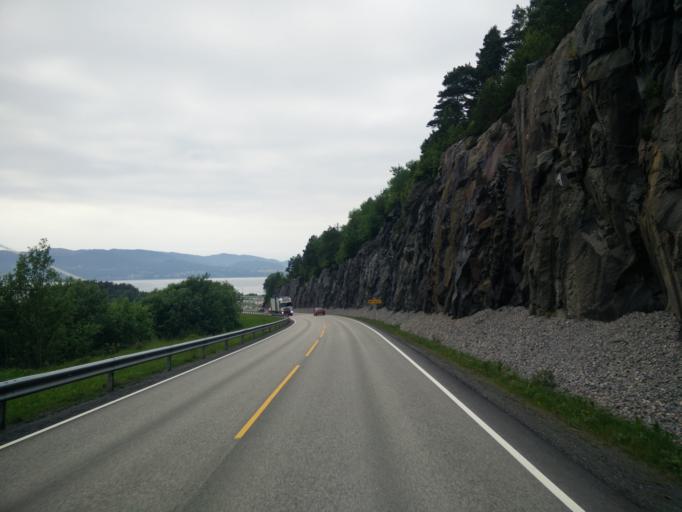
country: NO
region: More og Romsdal
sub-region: Kristiansund
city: Rensvik
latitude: 62.9723
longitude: 7.7944
